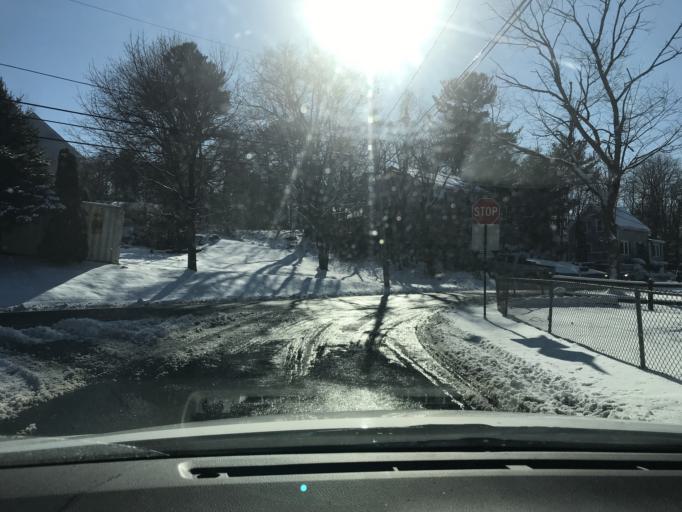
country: US
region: Massachusetts
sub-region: Essex County
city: Saugus
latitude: 42.4898
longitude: -71.0141
